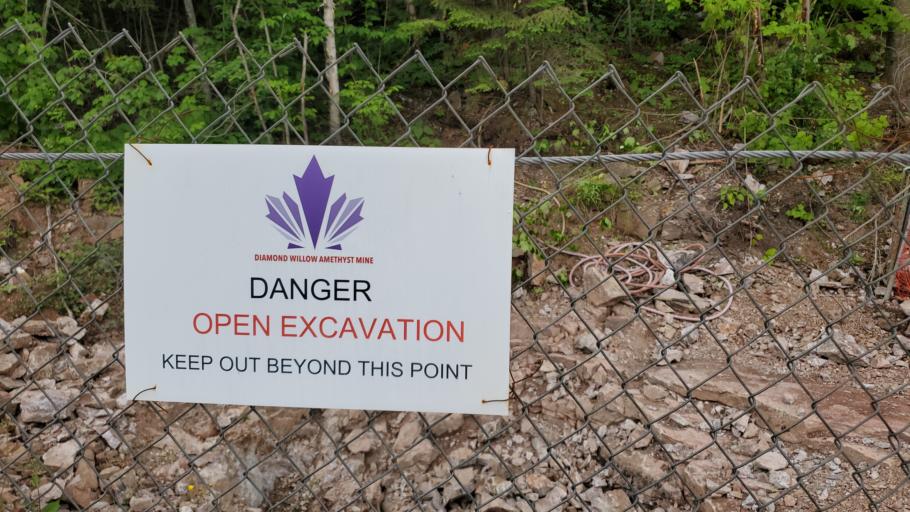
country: CA
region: Ontario
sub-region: Thunder Bay District
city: Thunder Bay
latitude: 48.6863
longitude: -88.6666
